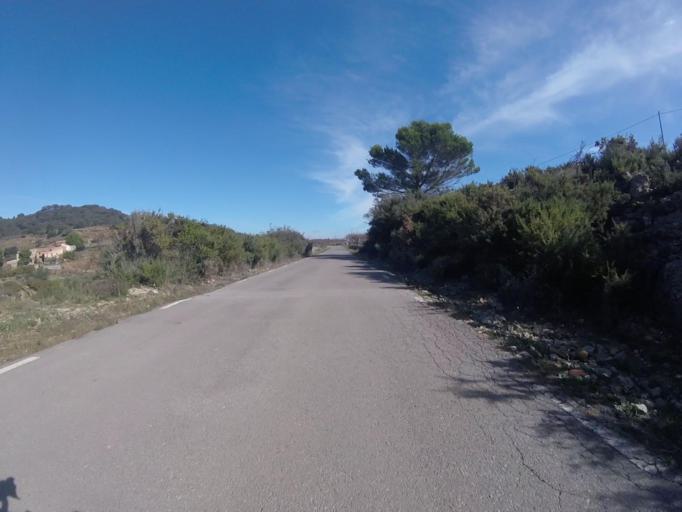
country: ES
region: Valencia
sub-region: Provincia de Castello
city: Sarratella
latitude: 40.3013
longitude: 0.0297
